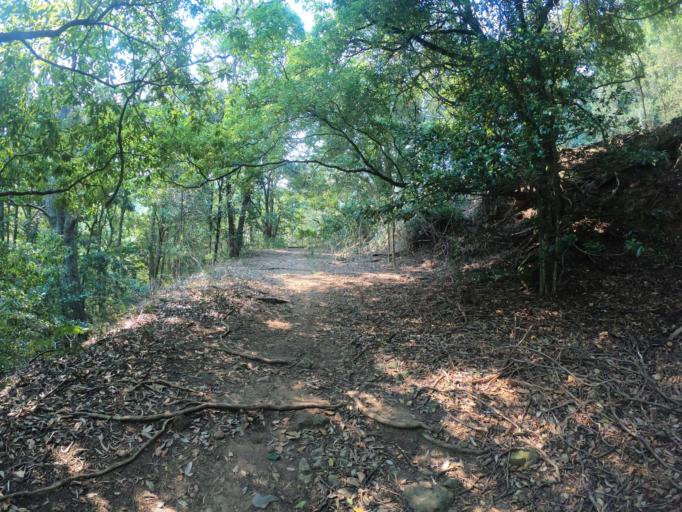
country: AU
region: New South Wales
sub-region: Wollongong
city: Bulli
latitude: -34.3233
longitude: 150.8884
